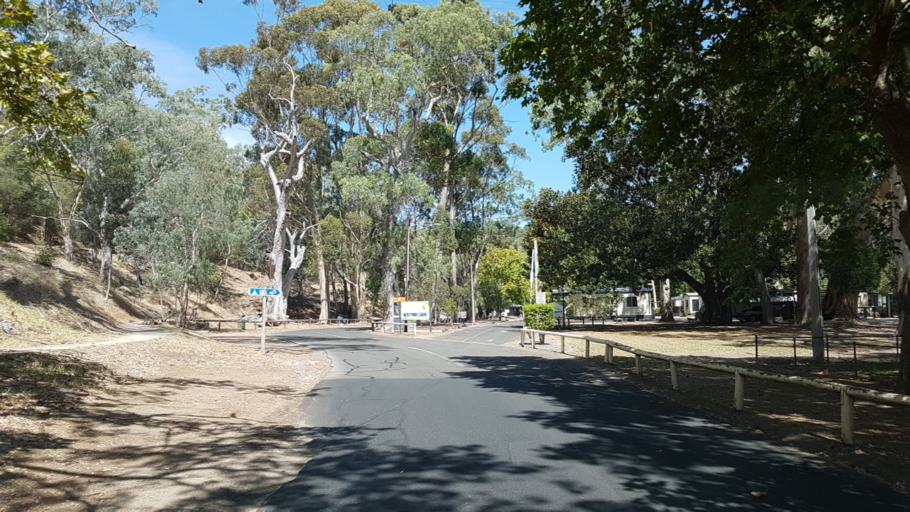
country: AU
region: South Australia
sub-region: Mitcham
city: Mitcham
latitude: -34.9844
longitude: 138.6266
